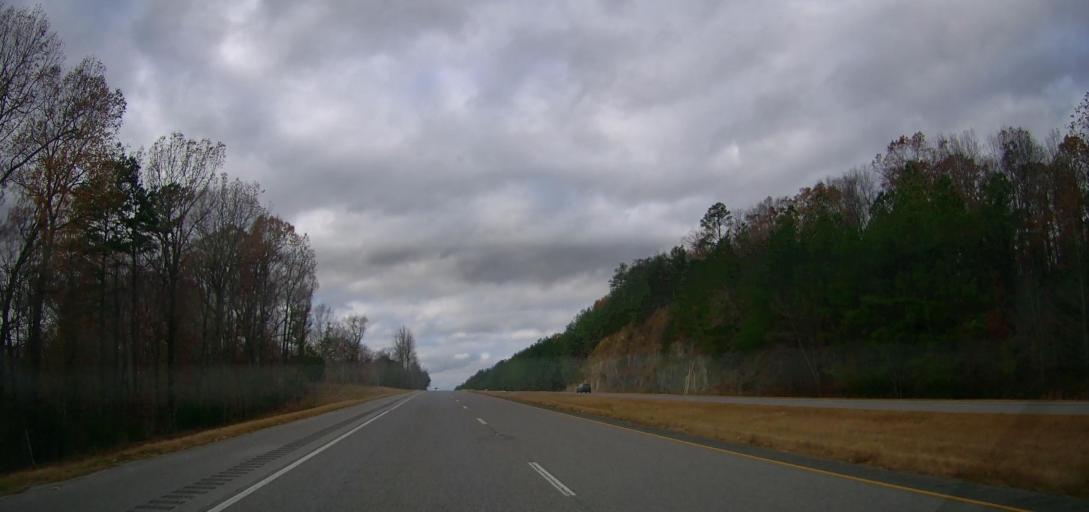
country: US
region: Alabama
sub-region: Lawrence County
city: Town Creek
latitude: 34.6157
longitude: -87.4627
